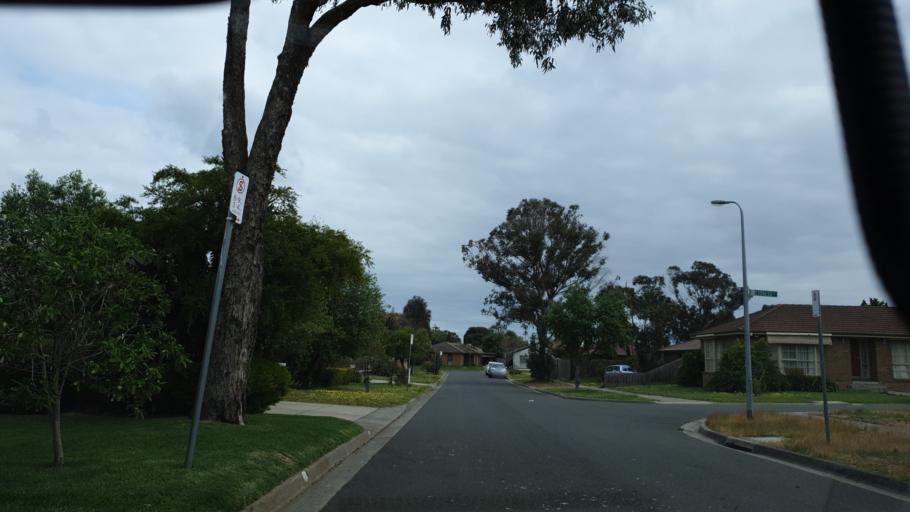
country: AU
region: Victoria
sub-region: Casey
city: Cranbourne North
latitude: -38.0782
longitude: 145.2839
